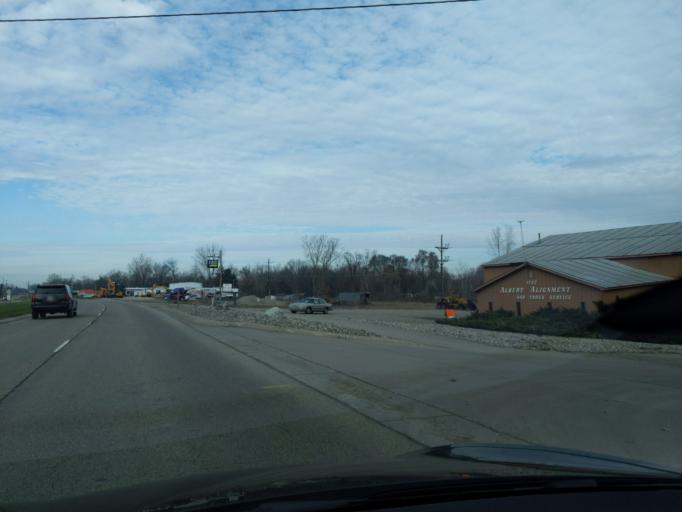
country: US
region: Michigan
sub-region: Ingham County
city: Holt
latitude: 42.6329
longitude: -84.5071
